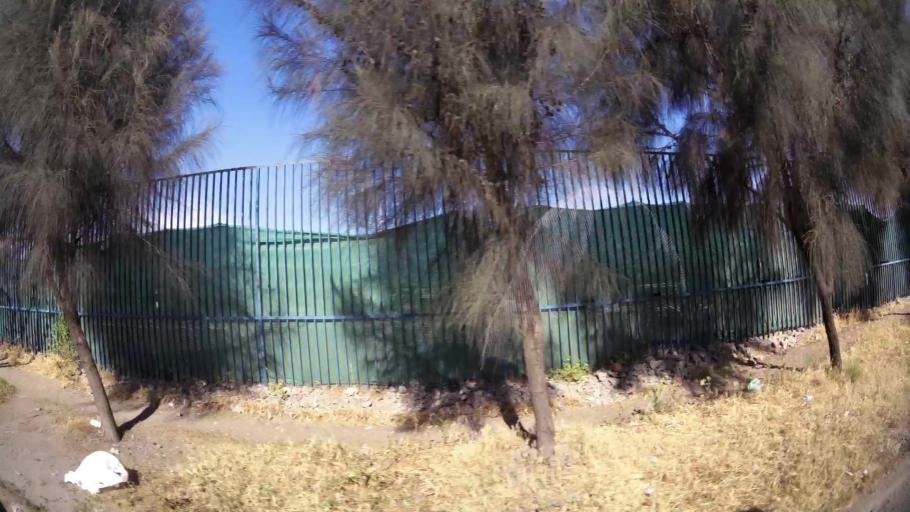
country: CL
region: Santiago Metropolitan
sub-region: Provincia de Santiago
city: Santiago
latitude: -33.5024
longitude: -70.6748
